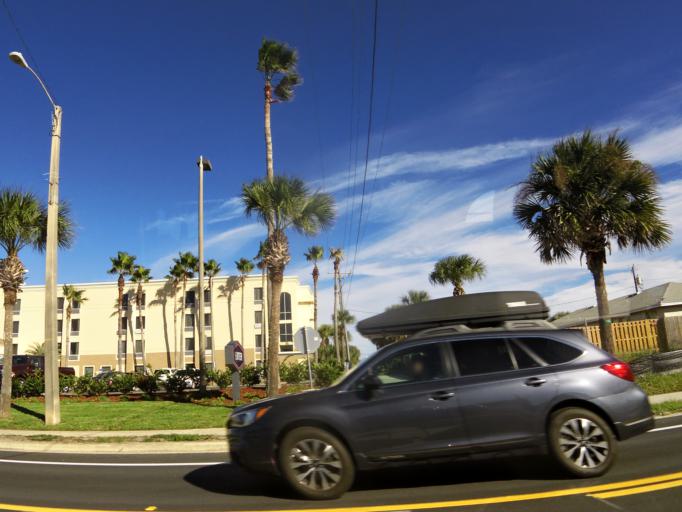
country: US
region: Florida
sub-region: Saint Johns County
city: Saint Augustine Beach
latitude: 29.8538
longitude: -81.2673
